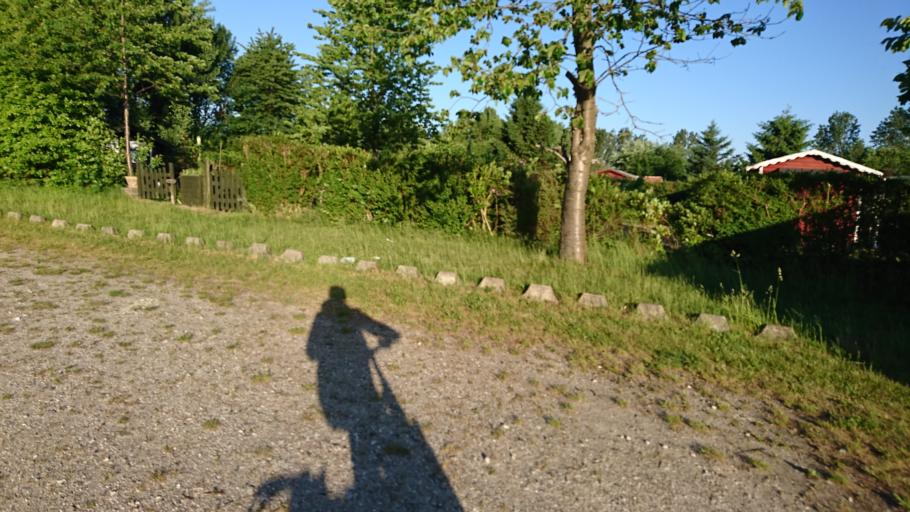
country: DK
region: Capital Region
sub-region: Egedal Kommune
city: Smorumnedre
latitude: 55.7285
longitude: 12.3239
